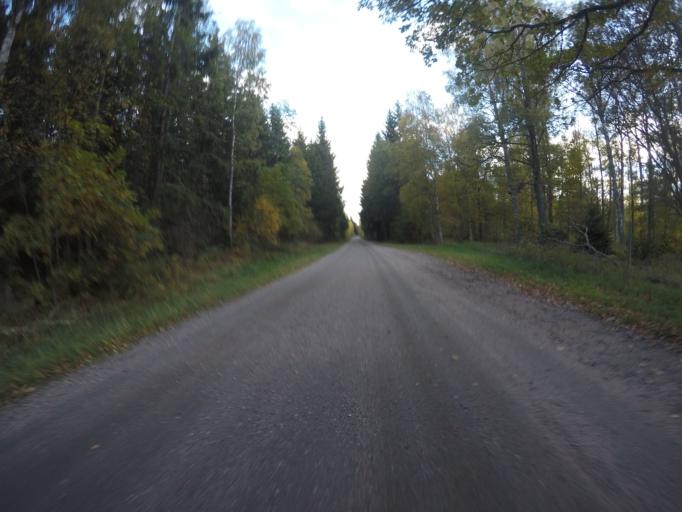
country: SE
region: Vaestmanland
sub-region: Arboga Kommun
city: Tyringe
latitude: 59.3343
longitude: 15.9661
